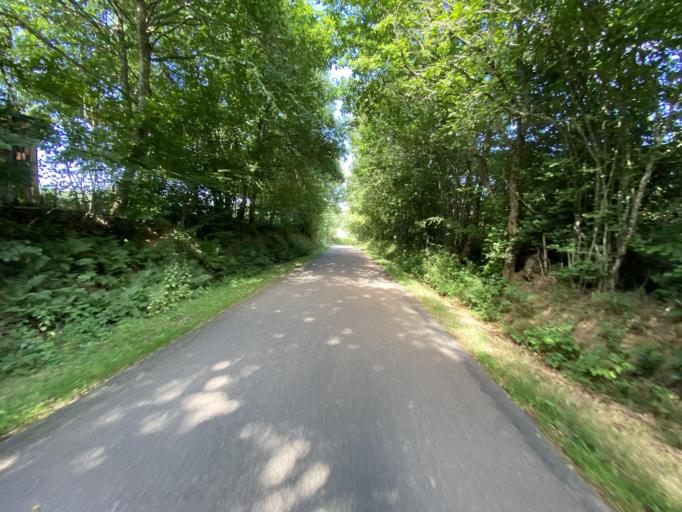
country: FR
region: Bourgogne
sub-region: Departement de la Cote-d'Or
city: Saulieu
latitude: 47.3233
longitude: 4.1544
